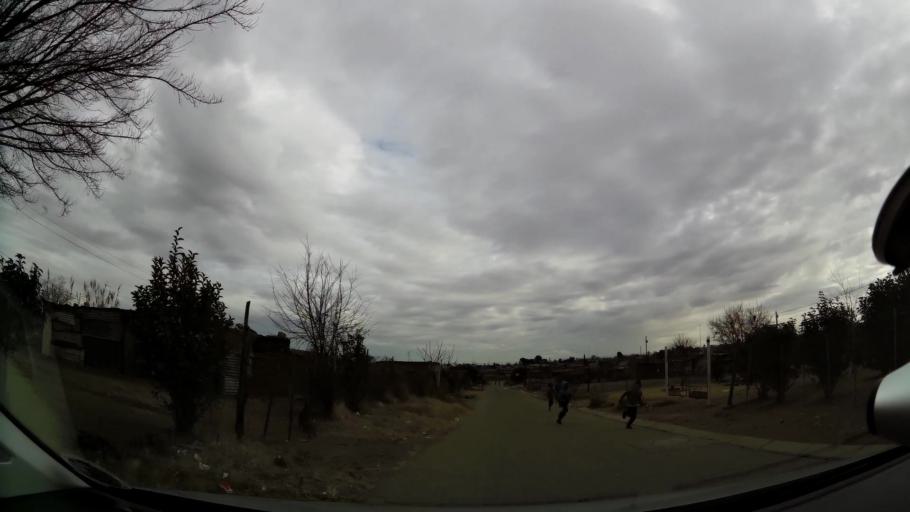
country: ZA
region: Orange Free State
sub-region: Fezile Dabi District Municipality
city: Kroonstad
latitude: -27.6475
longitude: 27.2159
